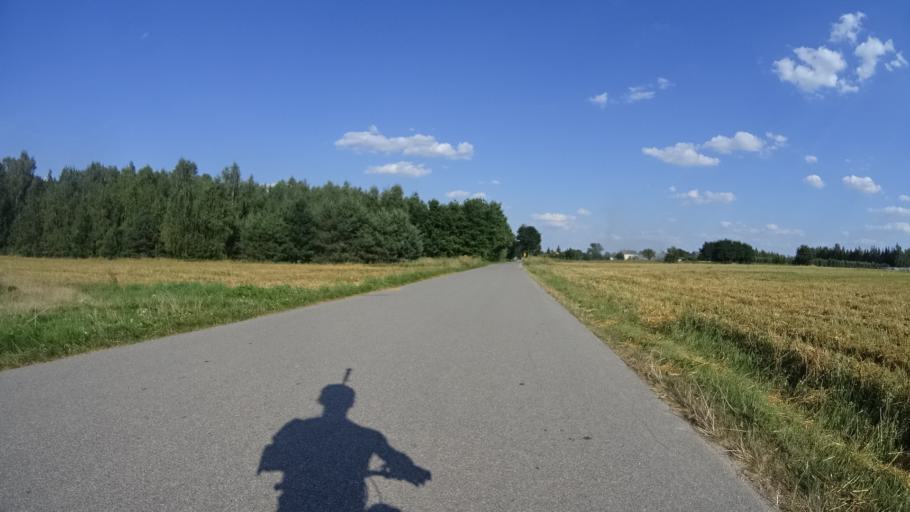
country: PL
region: Masovian Voivodeship
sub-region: Powiat bialobrzeski
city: Wysmierzyce
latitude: 51.6143
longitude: 20.8416
